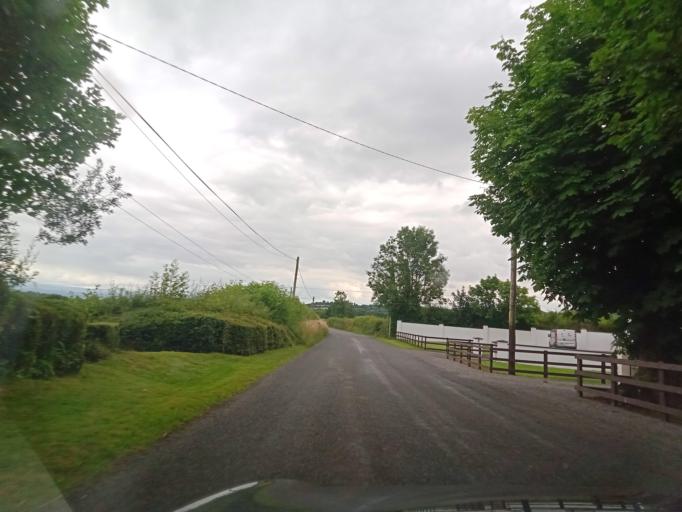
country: IE
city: Ballylinan
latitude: 52.9068
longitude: -7.0979
